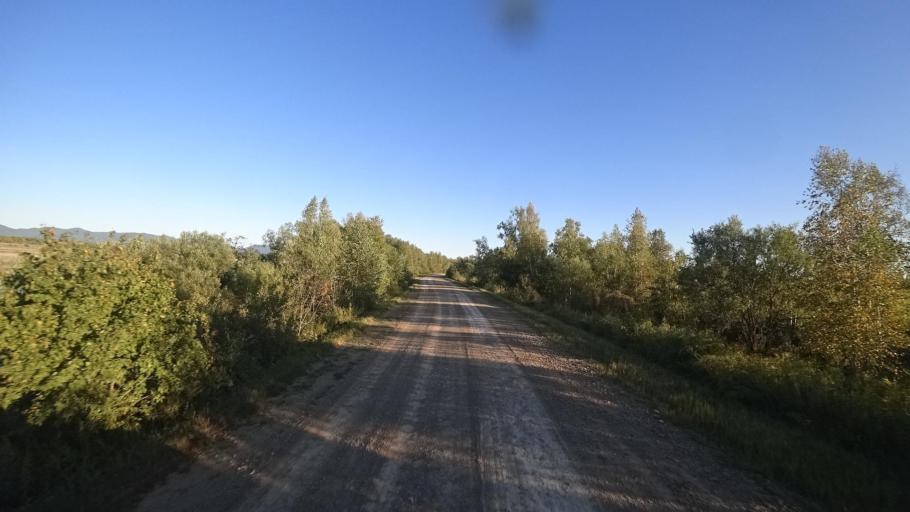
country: RU
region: Primorskiy
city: Kirovskiy
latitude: 44.7873
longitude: 133.6230
